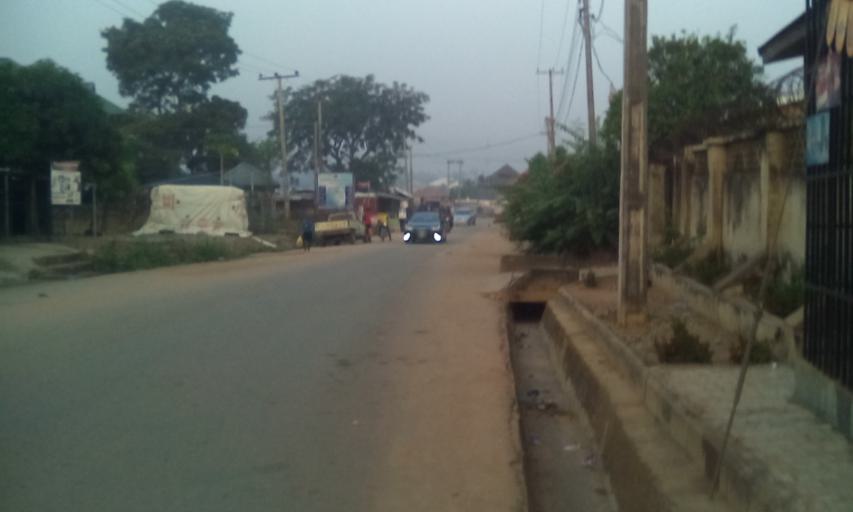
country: NG
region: Abuja Federal Capital Territory
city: Abuja
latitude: 8.9835
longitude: 7.3559
